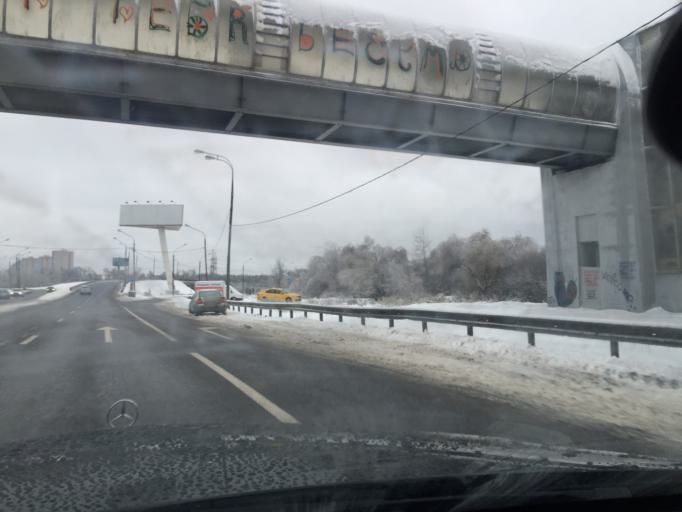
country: RU
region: Moscow
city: Khimki
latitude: 55.9236
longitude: 37.3946
